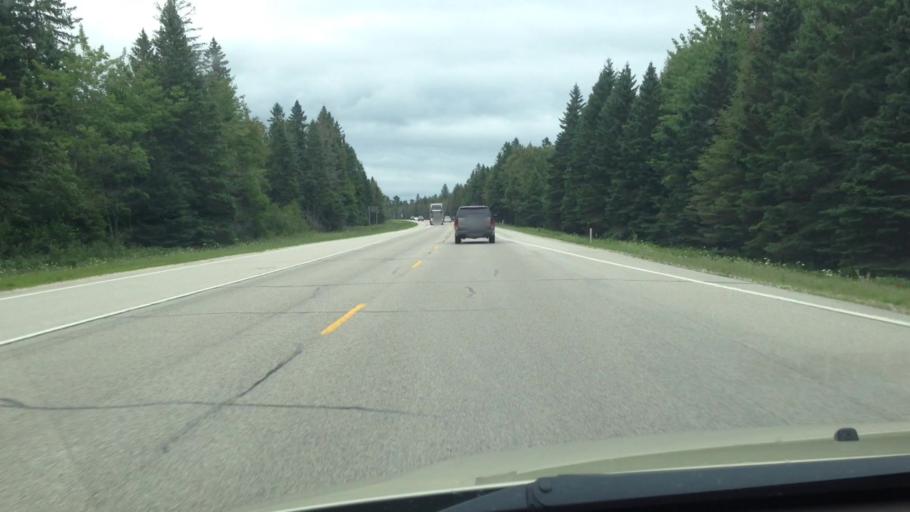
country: US
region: Michigan
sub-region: Luce County
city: Newberry
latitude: 46.0953
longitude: -85.3890
